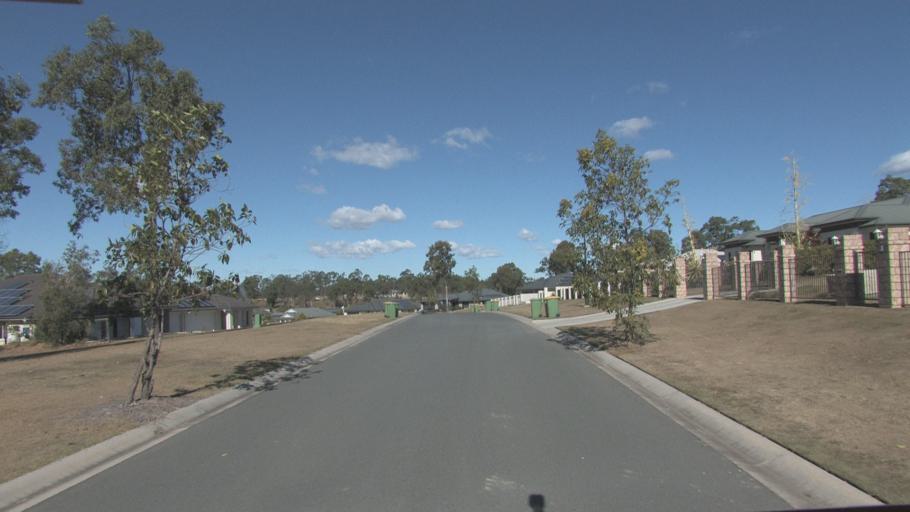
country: AU
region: Queensland
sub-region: Logan
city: North Maclean
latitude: -27.7551
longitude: 152.9464
